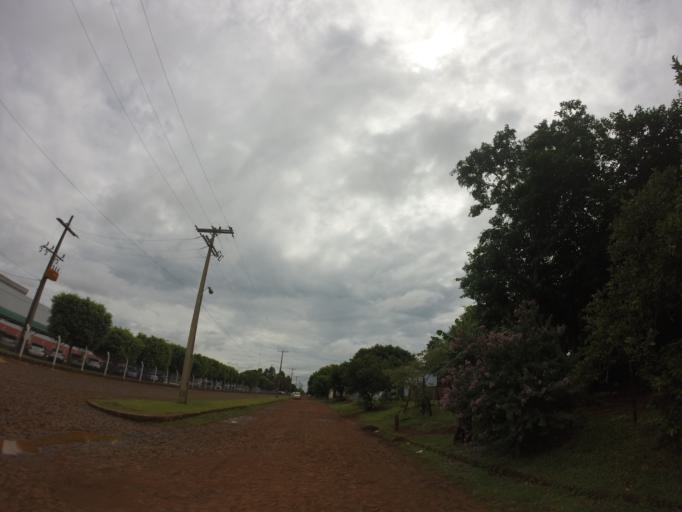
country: PY
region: Alto Parana
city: Ciudad del Este
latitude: -25.3850
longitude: -54.6622
